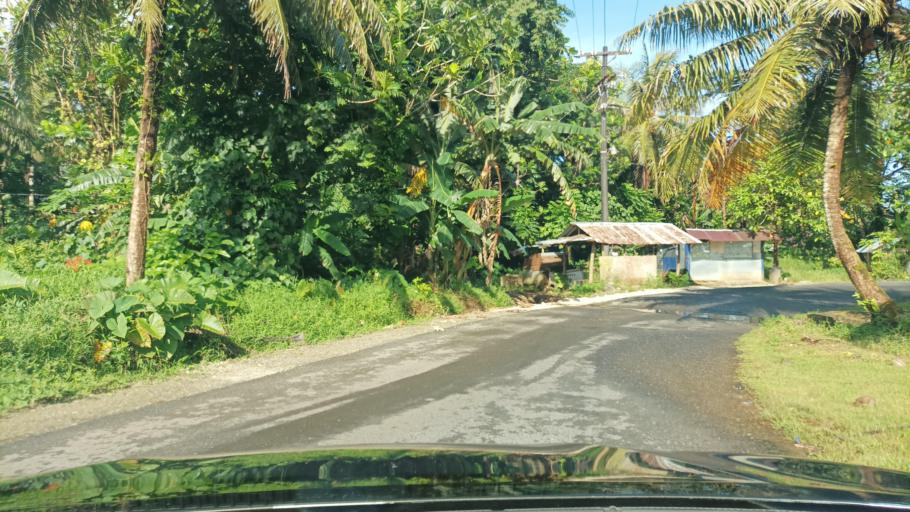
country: FM
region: Pohnpei
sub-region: Sokehs Municipality
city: Palikir - National Government Center
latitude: 6.9151
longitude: 158.1596
